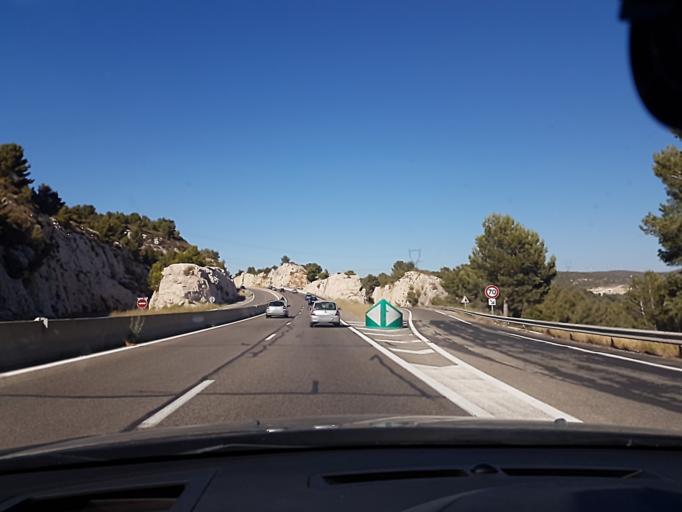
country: FR
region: Provence-Alpes-Cote d'Azur
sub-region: Departement des Bouches-du-Rhone
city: Ensues-la-Redonne
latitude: 43.3552
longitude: 5.1778
